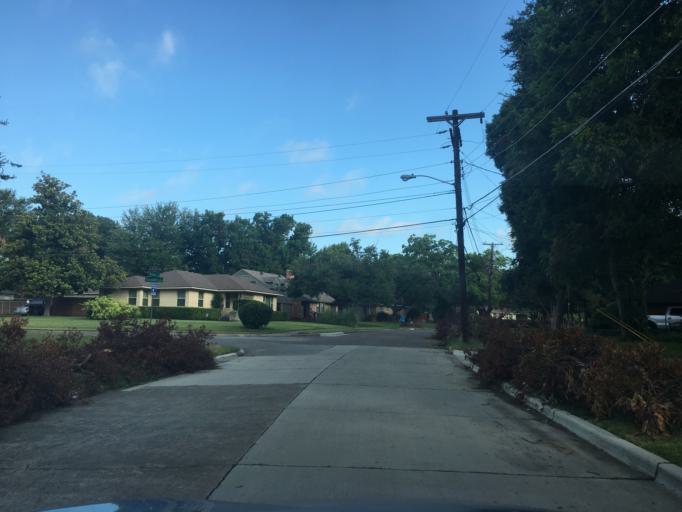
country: US
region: Texas
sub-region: Dallas County
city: Highland Park
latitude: 32.8486
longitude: -96.7480
